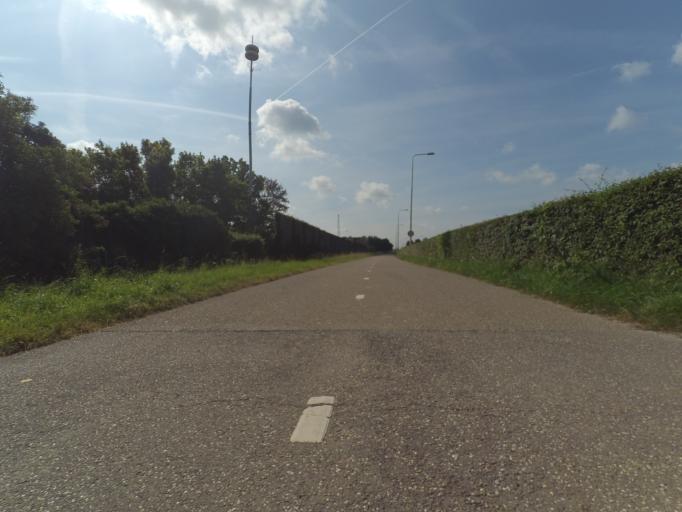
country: NL
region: Utrecht
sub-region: Gemeente Bunnik
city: Bunnik
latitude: 52.0506
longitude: 5.2285
